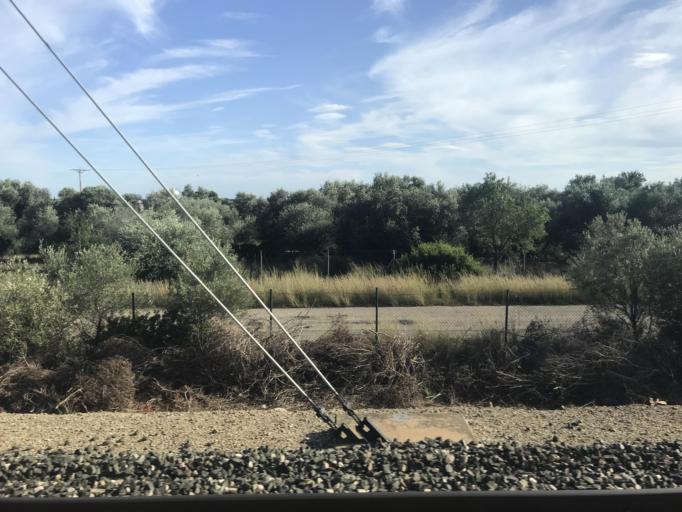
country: ES
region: Catalonia
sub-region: Provincia de Tarragona
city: Camarles
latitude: 40.7580
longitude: 0.6259
